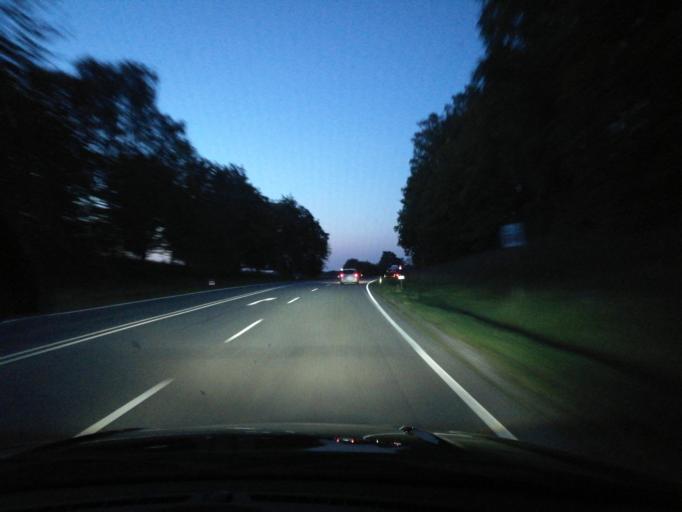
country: DE
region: Bavaria
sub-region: Lower Bavaria
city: Bad Abbach
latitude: 48.9497
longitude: 12.0430
